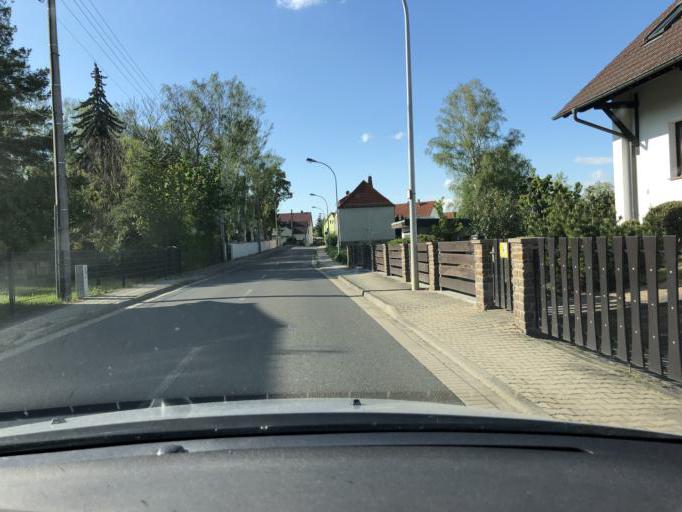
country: DE
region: Thuringia
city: Haselbach
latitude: 51.0828
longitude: 12.4291
